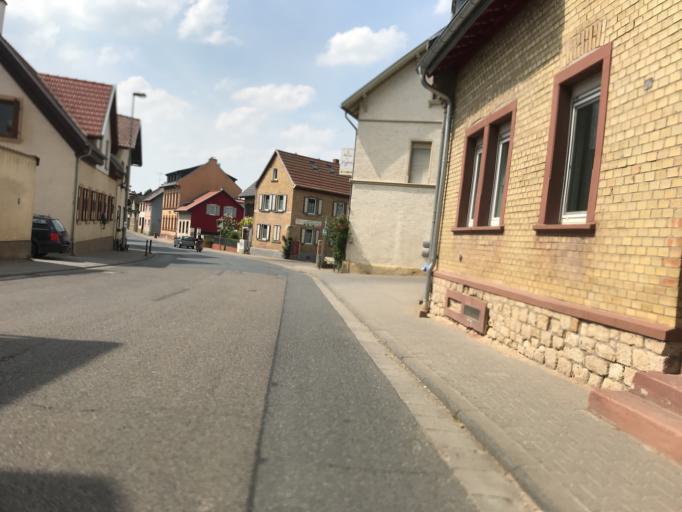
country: DE
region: Rheinland-Pfalz
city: Stadecken-Elsheim
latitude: 49.9091
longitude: 8.1366
